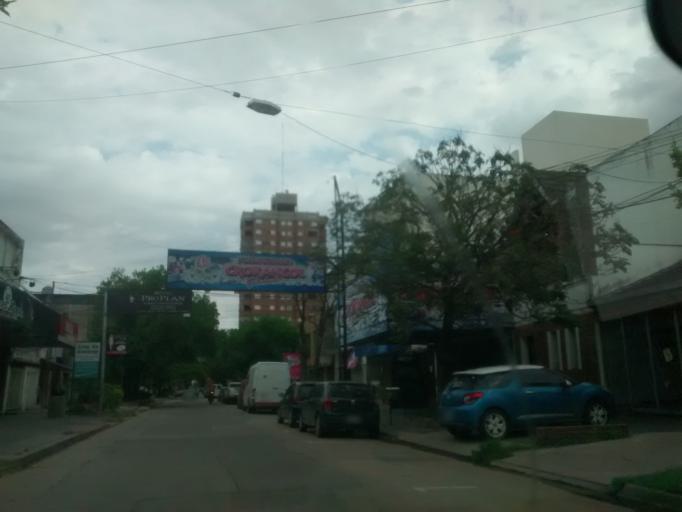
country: AR
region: Chaco
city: Resistencia
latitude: -27.4483
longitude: -58.9915
